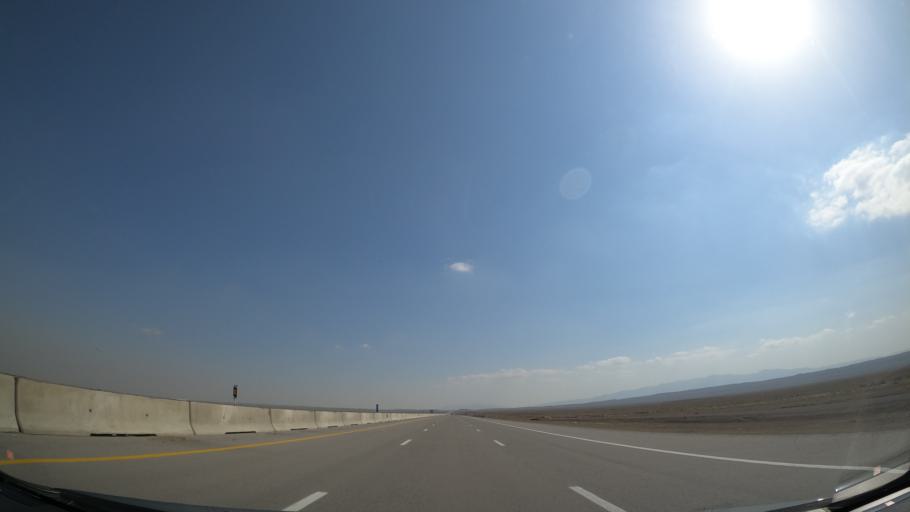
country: IR
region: Alborz
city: Nazarabad
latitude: 35.8305
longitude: 50.5006
